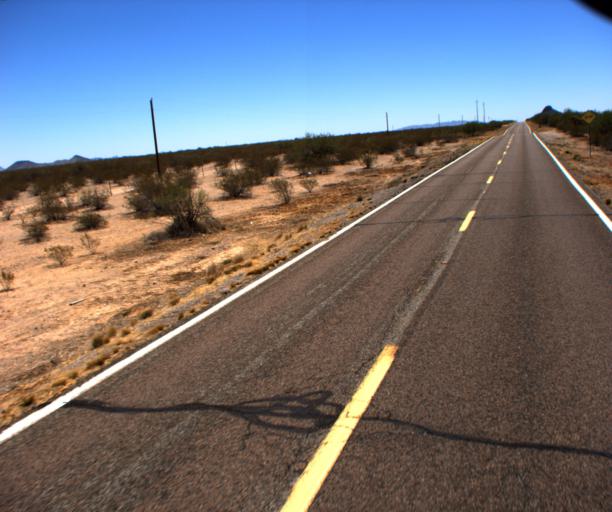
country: US
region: Arizona
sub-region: Pima County
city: Ajo
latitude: 32.2068
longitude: -112.5806
